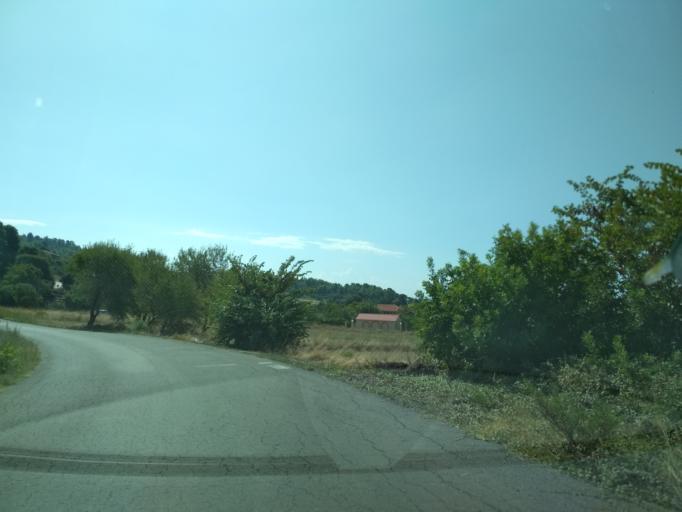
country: GR
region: Central Greece
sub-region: Nomos Evvoias
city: Roviai
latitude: 38.8206
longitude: 23.2669
